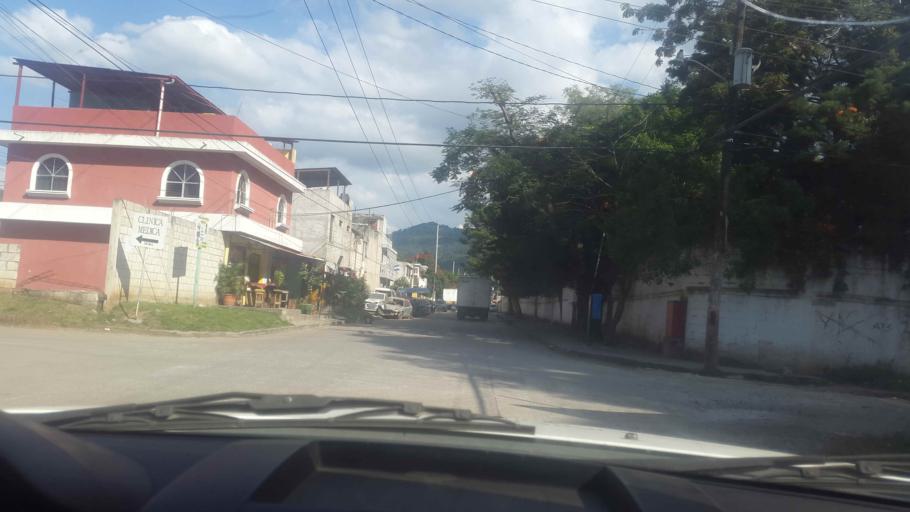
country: GT
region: Guatemala
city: Petapa
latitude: 14.5156
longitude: -90.5408
